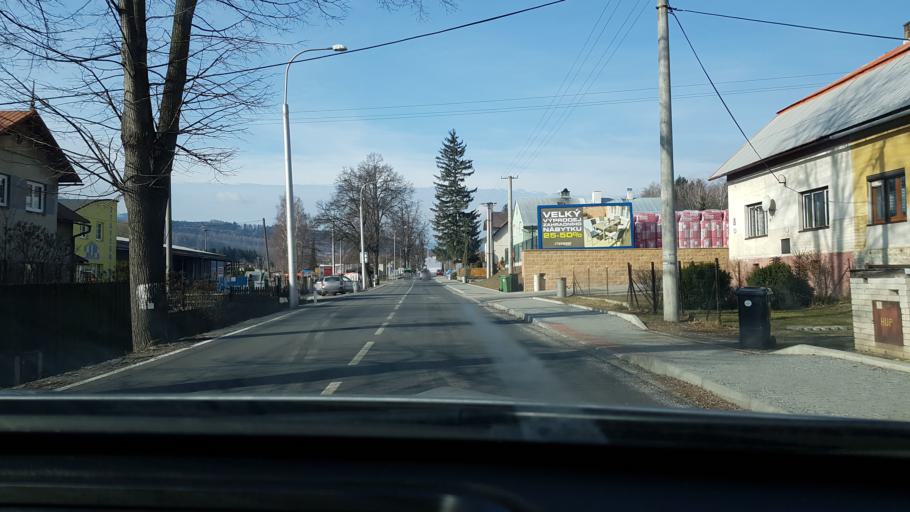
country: CZ
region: Olomoucky
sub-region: Okres Jesenik
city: Jesenik
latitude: 50.2270
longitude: 17.1861
